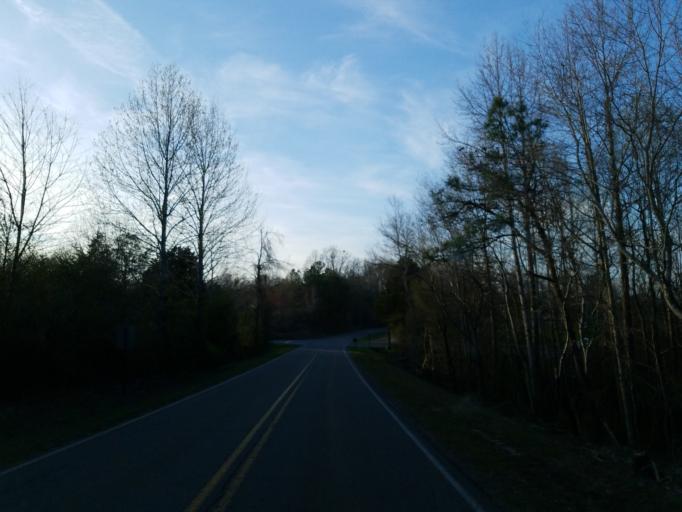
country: US
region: Georgia
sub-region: Pickens County
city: Jasper
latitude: 34.4873
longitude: -84.5132
